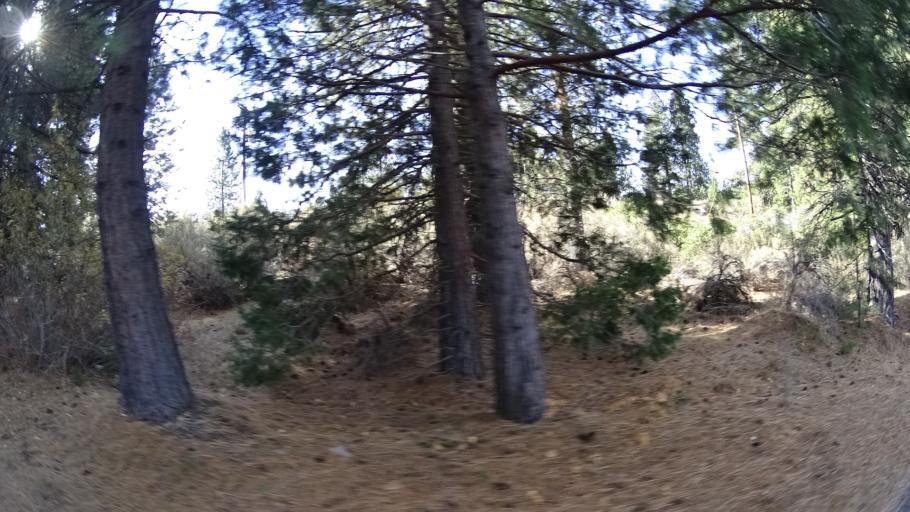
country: US
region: California
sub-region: Siskiyou County
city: Weed
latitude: 41.4257
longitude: -122.3966
